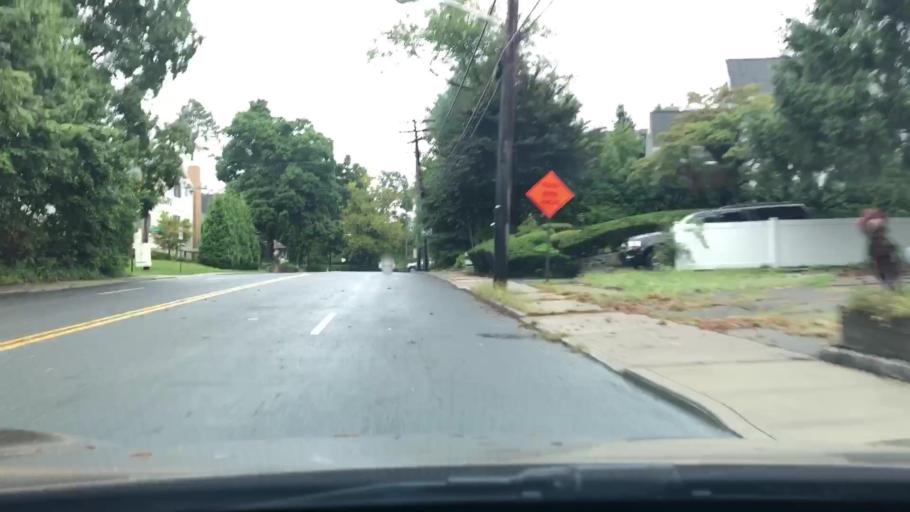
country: US
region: New York
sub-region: Westchester County
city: Greenville
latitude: 40.9772
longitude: -73.8023
